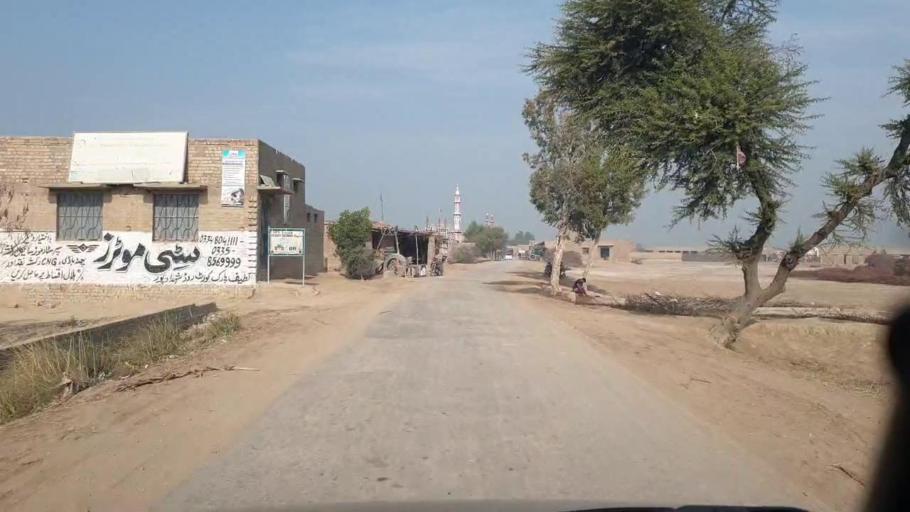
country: PK
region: Sindh
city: Shahdadpur
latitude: 25.9884
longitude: 68.5661
